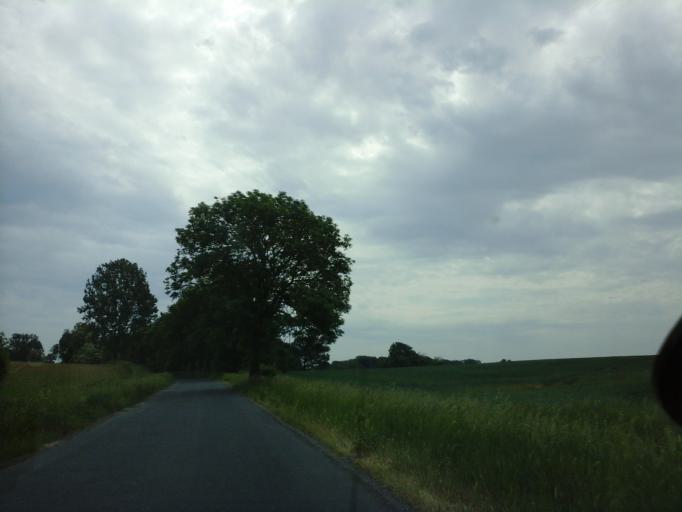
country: PL
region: West Pomeranian Voivodeship
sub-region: Powiat choszczenski
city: Krzecin
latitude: 53.1561
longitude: 15.5204
